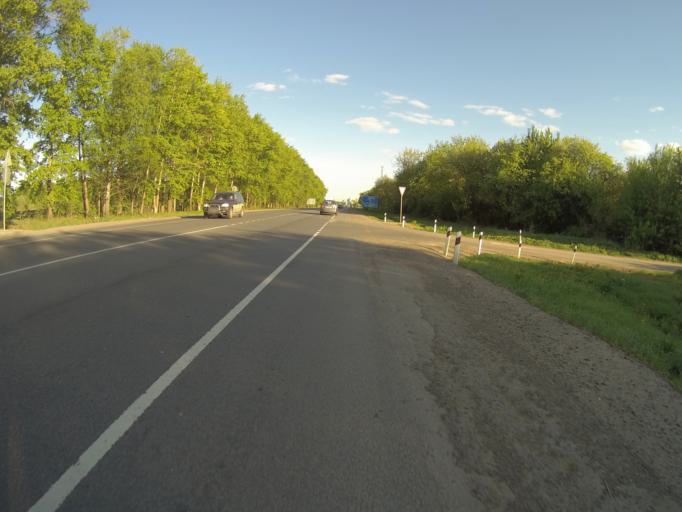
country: RU
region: Vladimir
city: Kommunar
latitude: 56.1821
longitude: 40.4503
